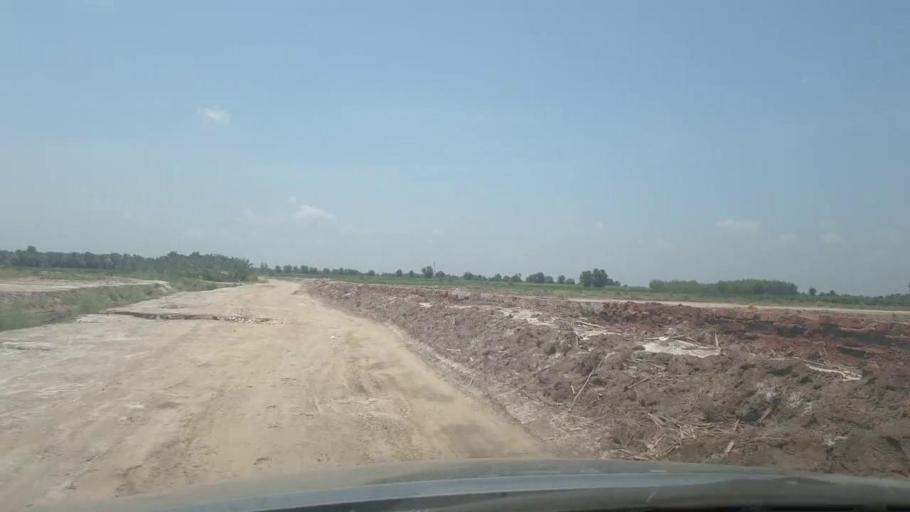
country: PK
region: Sindh
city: Kot Diji
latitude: 27.3875
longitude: 68.6959
